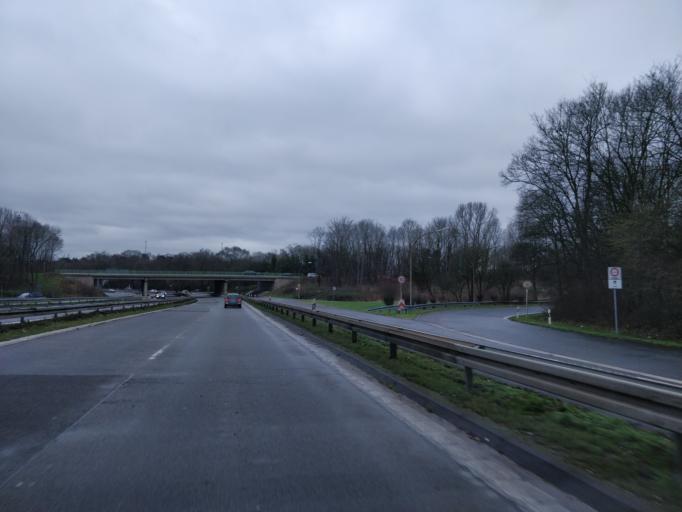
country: DE
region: North Rhine-Westphalia
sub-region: Regierungsbezirk Koln
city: Humboldtkolonie
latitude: 50.9319
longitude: 6.9846
